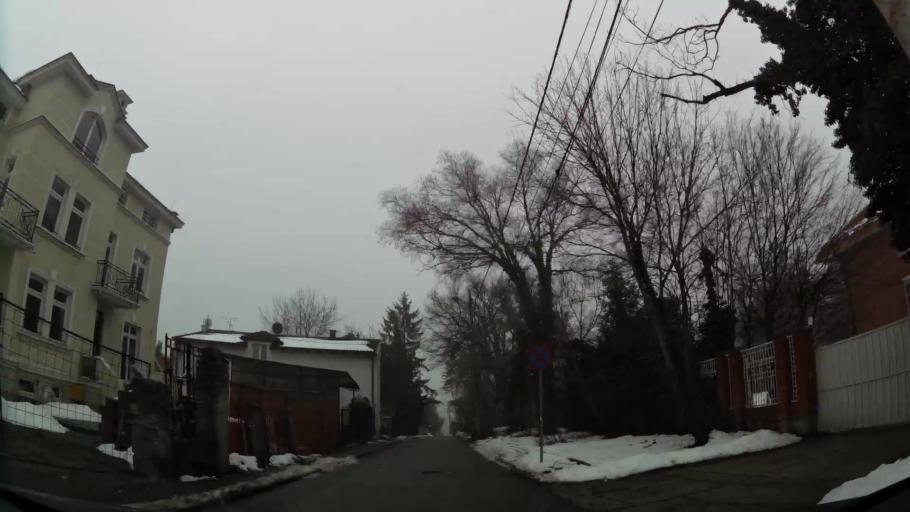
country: RS
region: Central Serbia
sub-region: Belgrade
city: Cukarica
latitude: 44.7882
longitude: 20.4366
